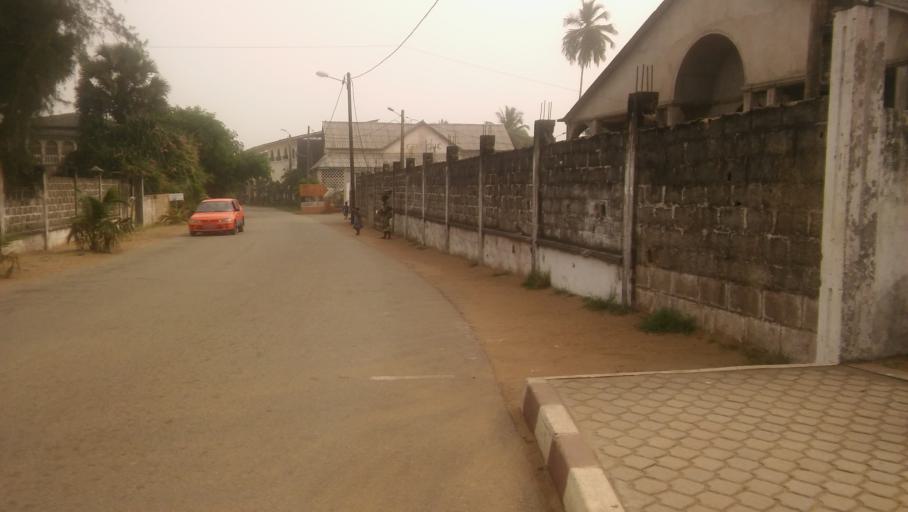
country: CI
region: Sud-Comoe
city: Grand-Bassam
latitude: 5.1947
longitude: -3.7327
